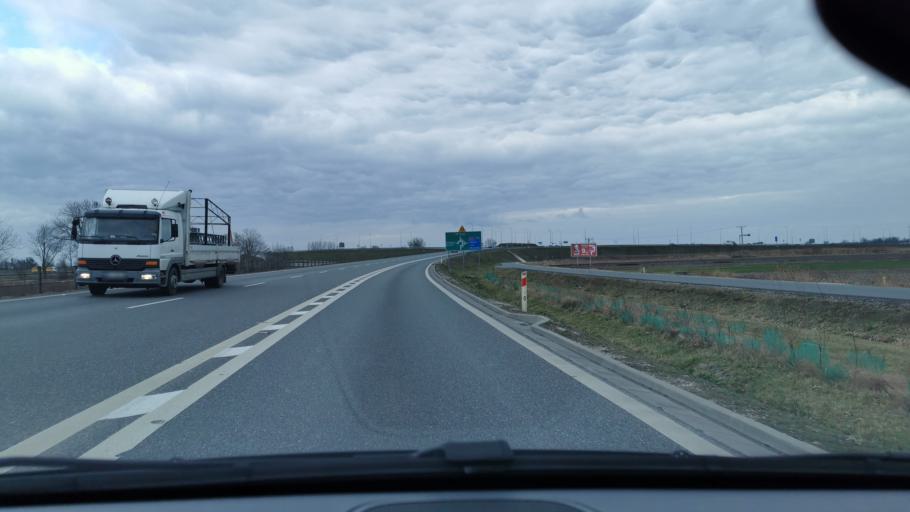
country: PL
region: Masovian Voivodeship
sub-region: Powiat zyrardowski
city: Wiskitki
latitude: 52.0947
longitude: 20.3625
